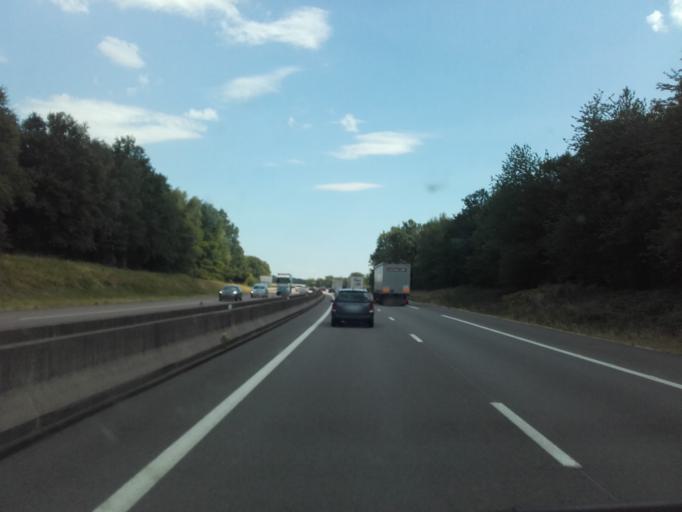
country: FR
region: Bourgogne
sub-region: Departement de la Cote-d'Or
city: Semur-en-Auxois
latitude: 47.4542
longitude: 4.2651
